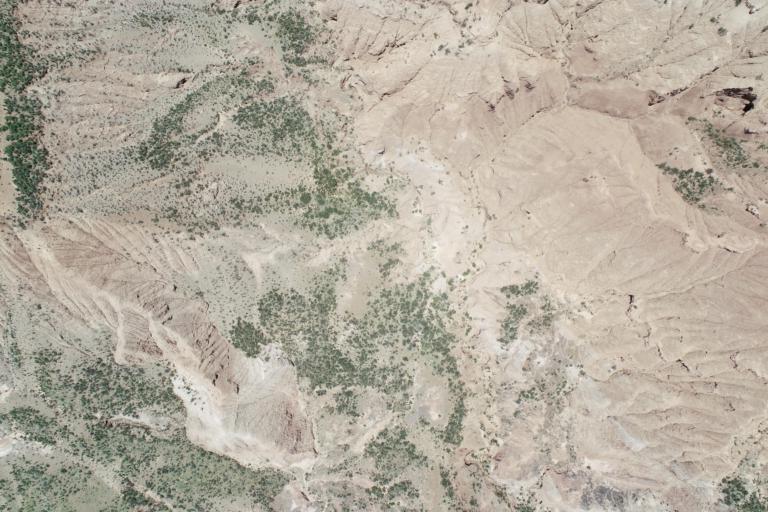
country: BO
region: La Paz
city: Curahuara de Carangas
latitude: -17.3053
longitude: -68.4992
